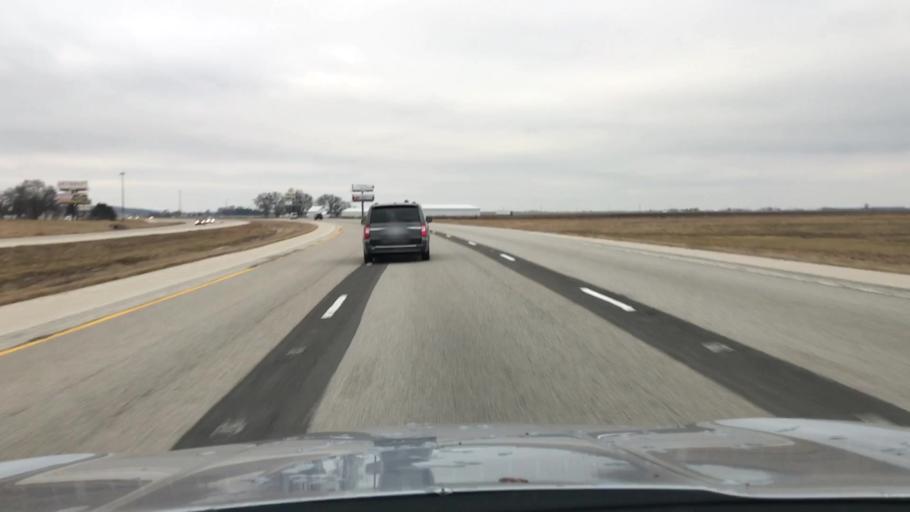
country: US
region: Illinois
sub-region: Logan County
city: Lincoln
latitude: 40.0739
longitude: -89.4431
